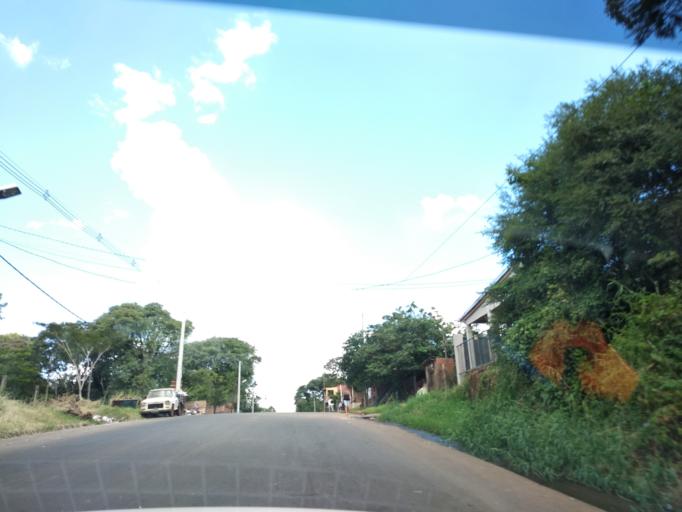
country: AR
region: Misiones
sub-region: Departamento de Capital
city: Posadas
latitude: -27.3558
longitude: -55.9150
